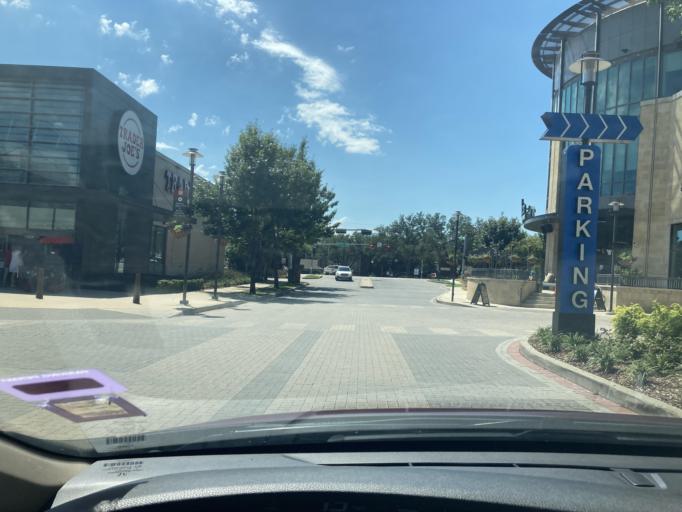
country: US
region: Texas
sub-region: Dallas County
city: University Park
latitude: 32.8813
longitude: -96.7728
